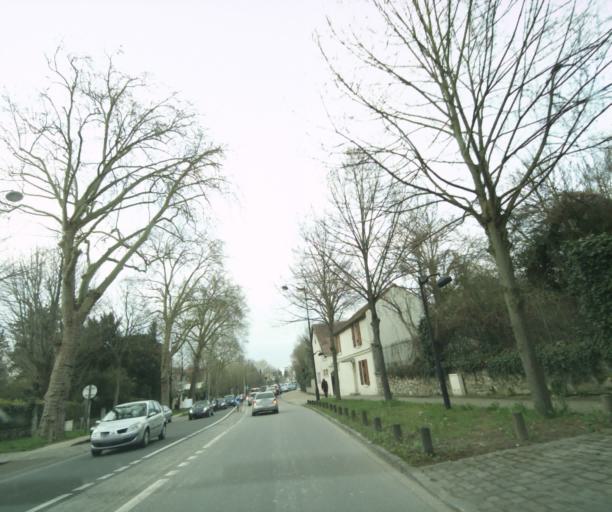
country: FR
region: Ile-de-France
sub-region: Departement des Yvelines
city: Louveciennes
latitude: 48.8719
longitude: 2.1021
